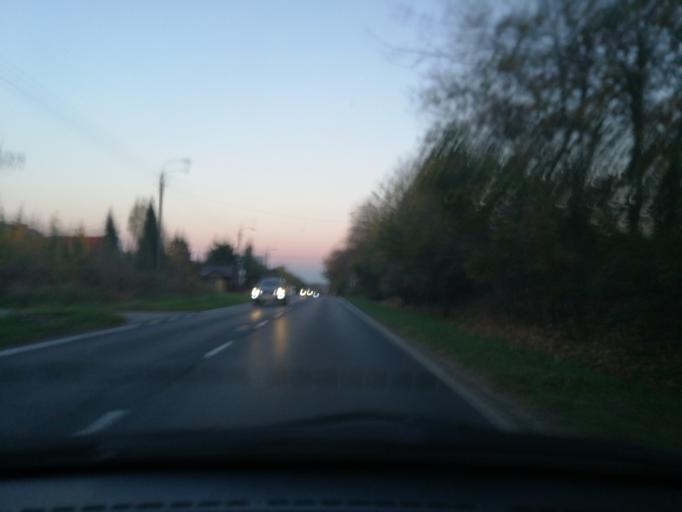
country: PL
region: Lodz Voivodeship
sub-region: Powiat lodzki wschodni
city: Andrespol
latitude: 51.7945
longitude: 19.5791
